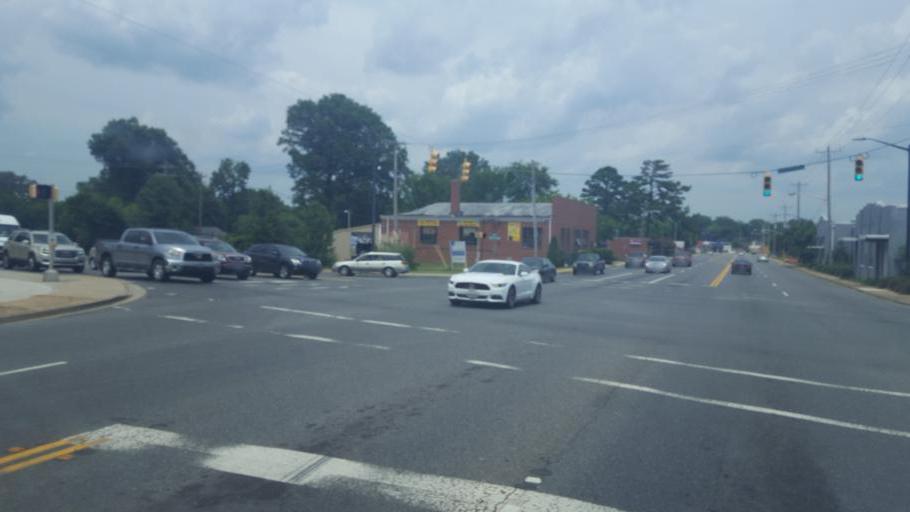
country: US
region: South Carolina
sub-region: York County
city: Rock Hill
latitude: 34.9388
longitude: -81.0400
